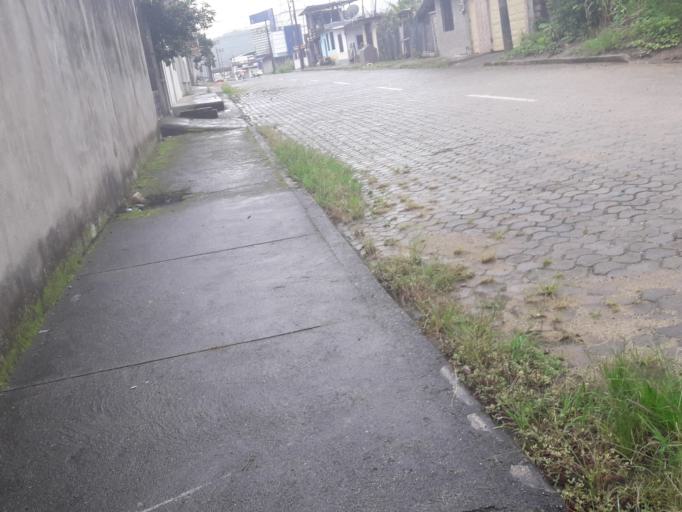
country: EC
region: Napo
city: Tena
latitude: -0.9875
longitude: -77.8221
